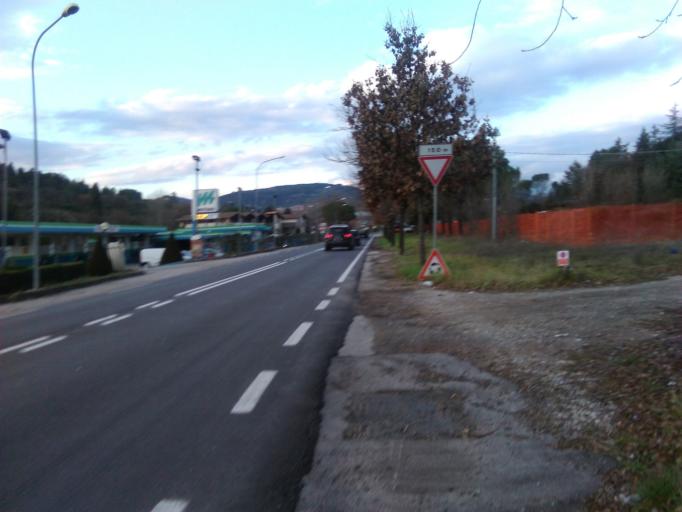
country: IT
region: Umbria
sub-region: Provincia di Perugia
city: Lacugnano
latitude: 43.0920
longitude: 12.3580
